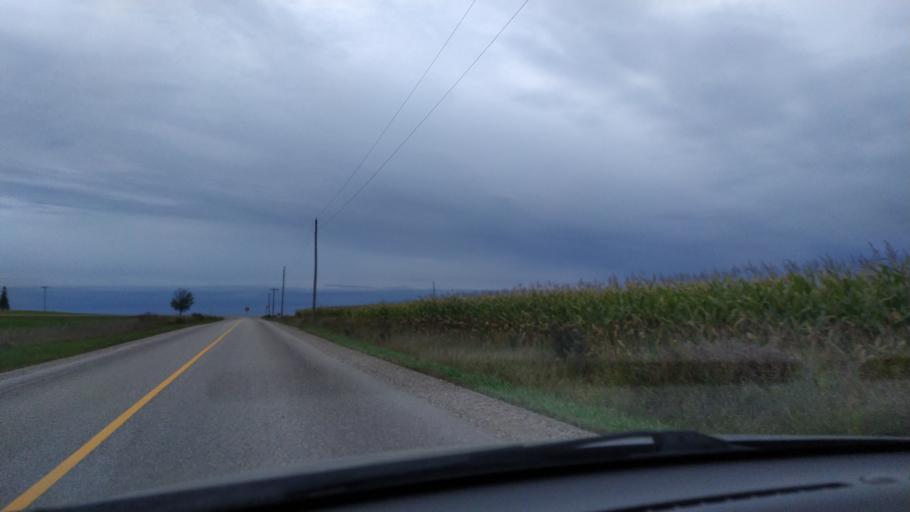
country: CA
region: Ontario
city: Waterloo
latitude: 43.5135
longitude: -80.7518
